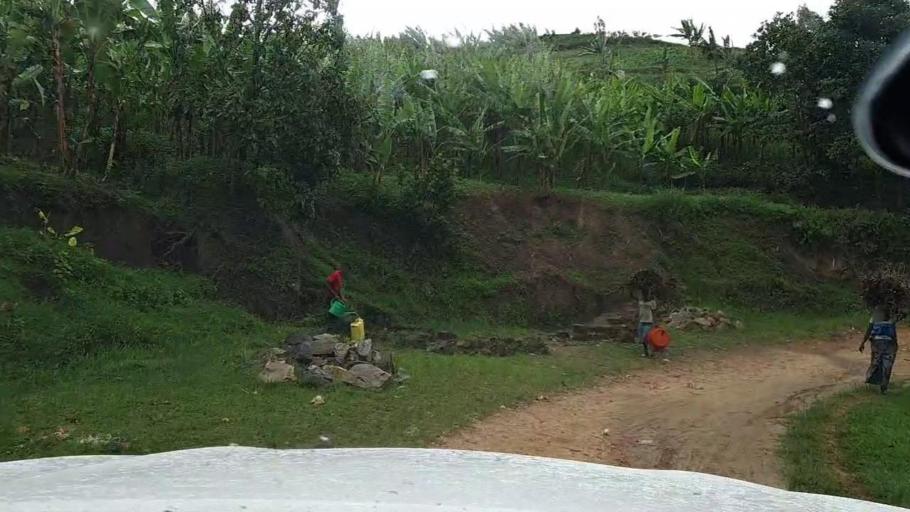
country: RW
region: Western Province
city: Kibuye
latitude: -2.0790
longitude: 29.4463
